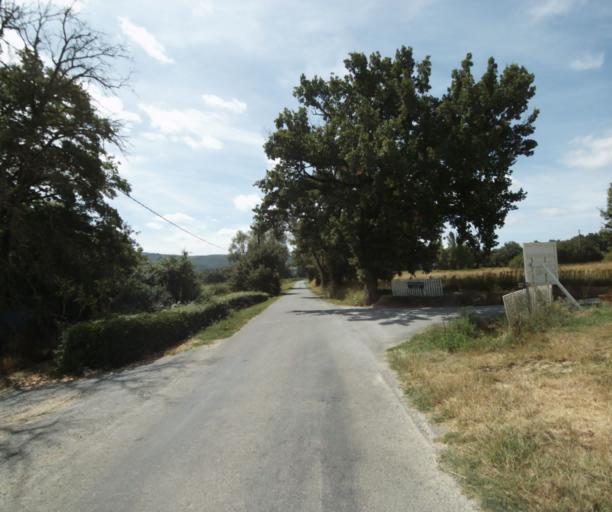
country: FR
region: Midi-Pyrenees
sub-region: Departement du Tarn
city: Soreze
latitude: 43.4862
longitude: 2.0776
